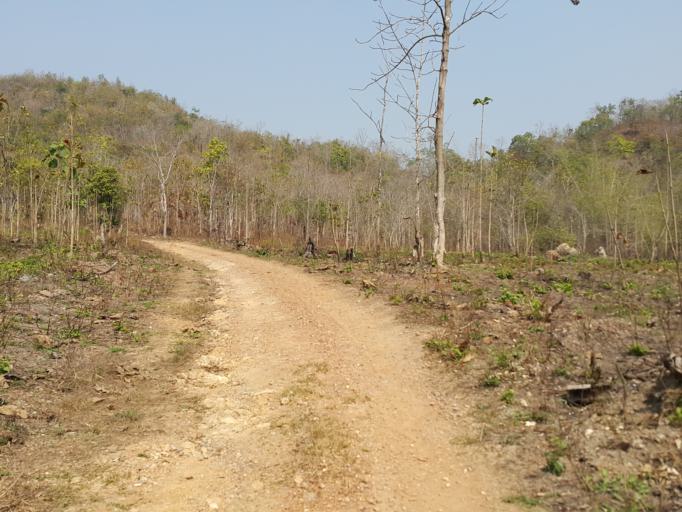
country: TH
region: Sukhothai
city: Thung Saliam
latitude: 17.3192
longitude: 99.5013
